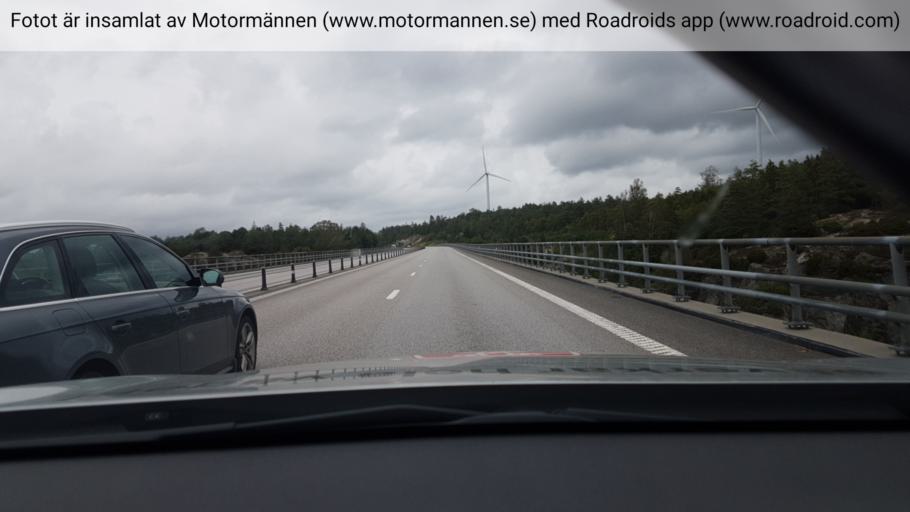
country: SE
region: Vaestra Goetaland
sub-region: Tanums Kommun
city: Tanumshede
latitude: 58.6450
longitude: 11.4349
